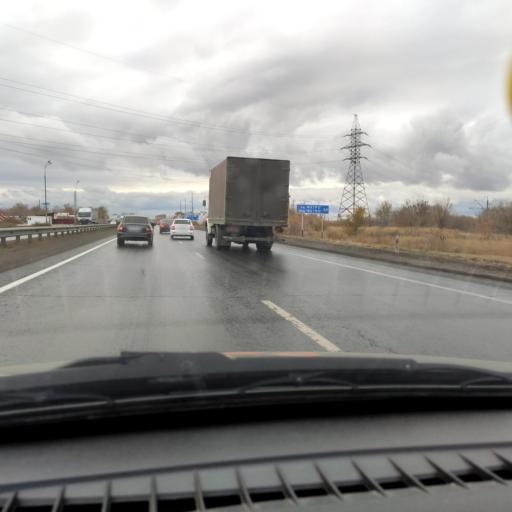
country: RU
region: Samara
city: Tol'yatti
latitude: 53.5626
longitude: 49.3638
